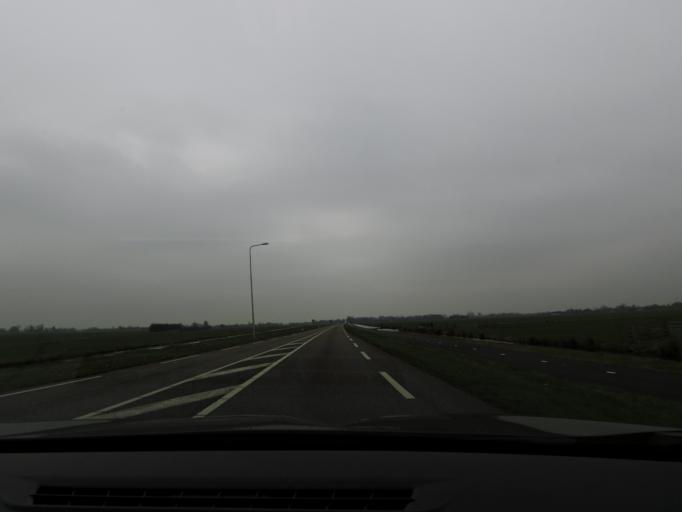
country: NL
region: Utrecht
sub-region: Gemeente Woerden
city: Woerden
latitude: 52.1433
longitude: 4.9116
